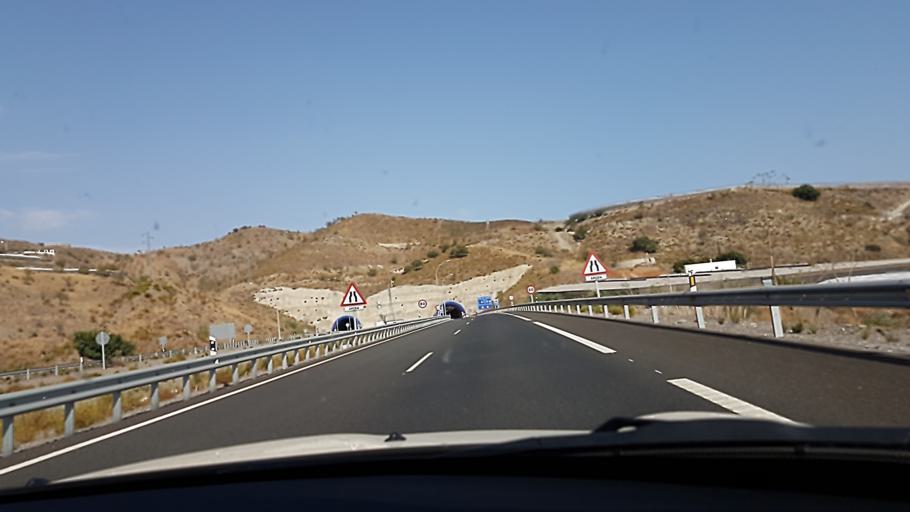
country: ES
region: Andalusia
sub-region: Provincia de Granada
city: Polopos
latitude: 36.7506
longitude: -3.3039
